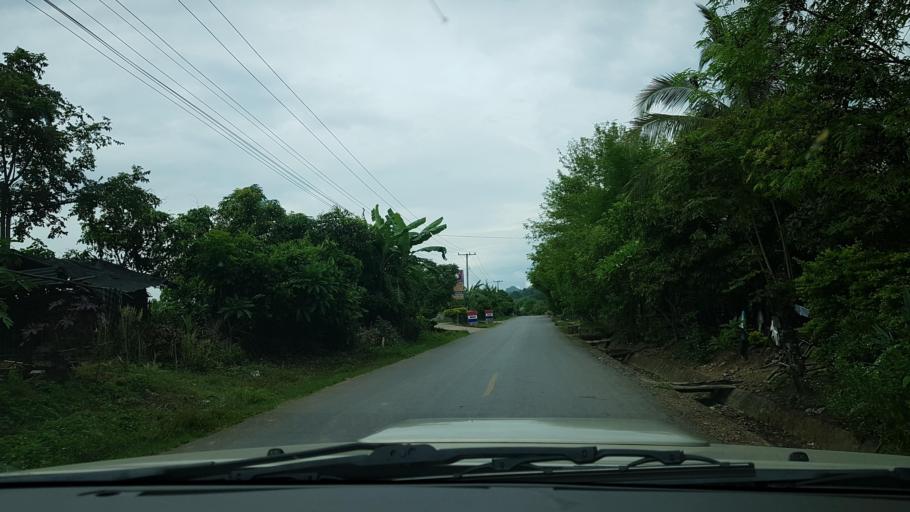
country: LA
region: Loungnamtha
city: Muang Nale
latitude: 20.3427
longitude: 101.6780
